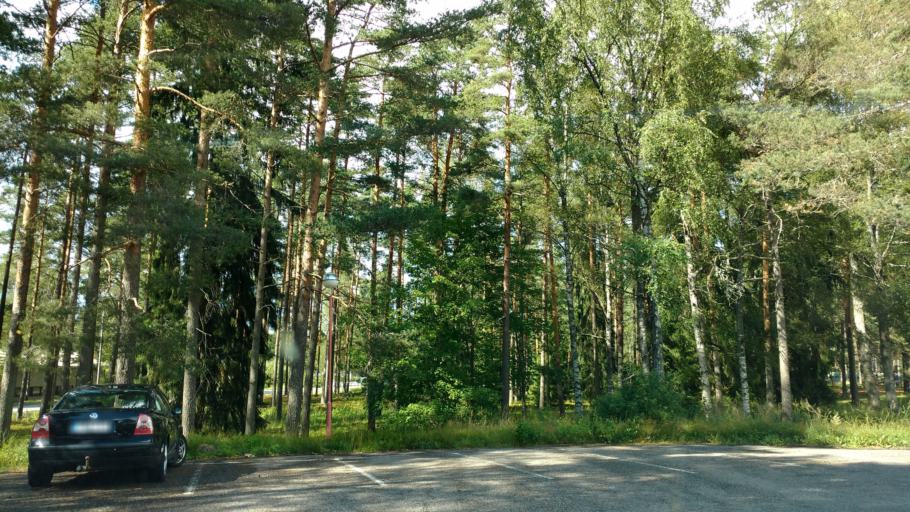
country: FI
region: Varsinais-Suomi
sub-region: Turku
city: Paimio
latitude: 60.4653
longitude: 22.7329
